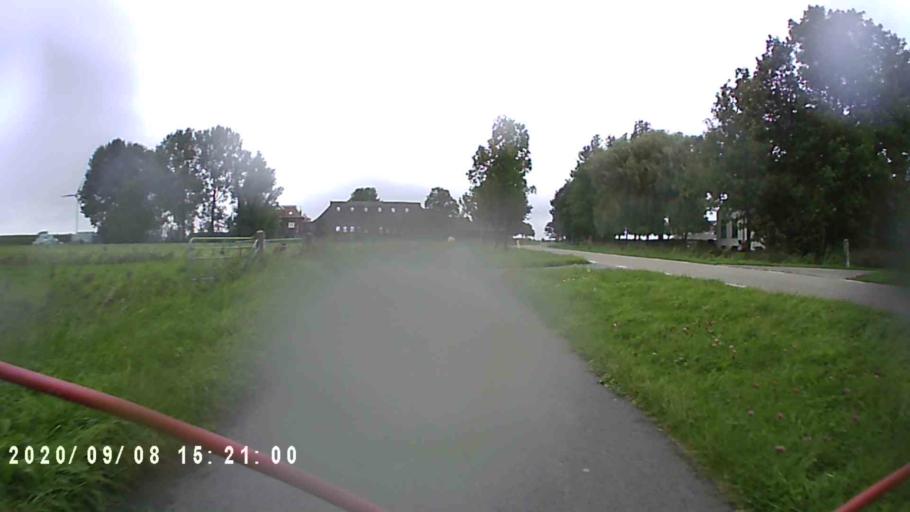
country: NL
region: Groningen
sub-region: Gemeente Bedum
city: Bedum
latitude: 53.2849
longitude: 6.6857
